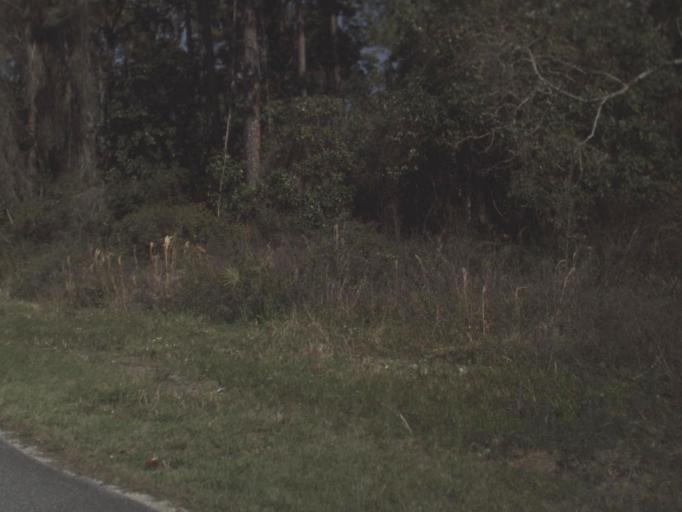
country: US
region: Florida
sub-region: Franklin County
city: Carrabelle
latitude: 29.8244
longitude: -84.7054
